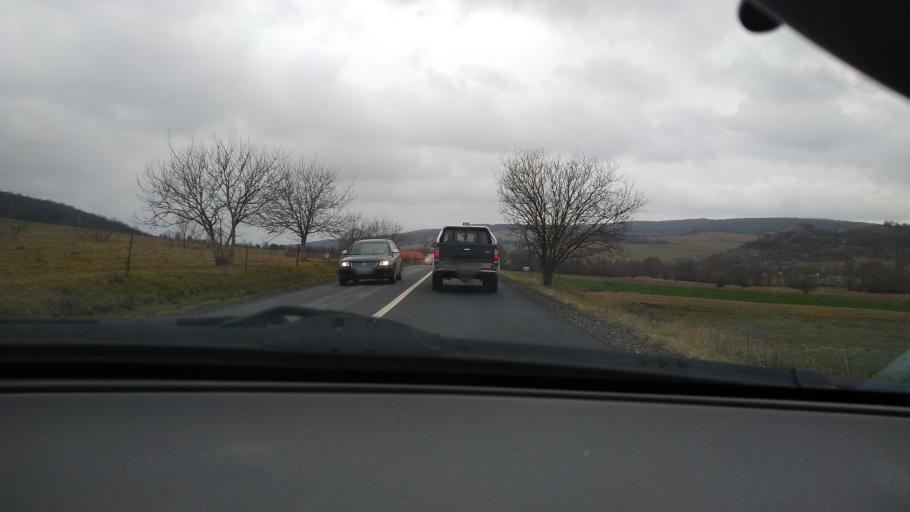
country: RO
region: Mures
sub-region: Comuna Bereni
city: Bereni
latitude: 46.5585
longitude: 24.8784
